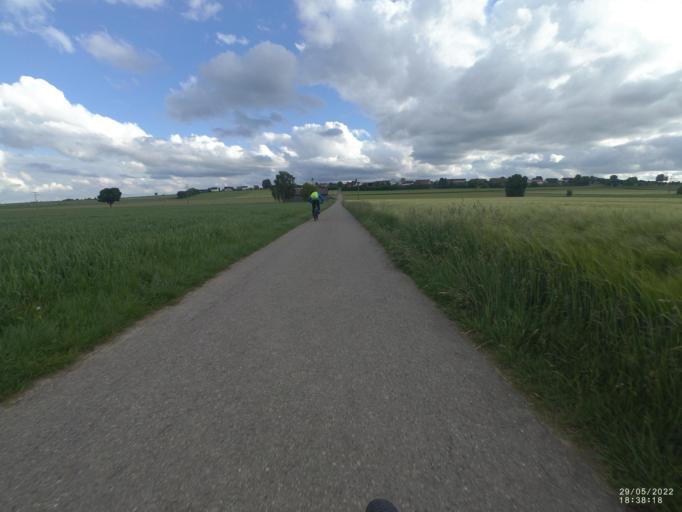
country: DE
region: Baden-Wuerttemberg
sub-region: Tuebingen Region
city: Ballendorf
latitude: 48.5985
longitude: 10.1066
